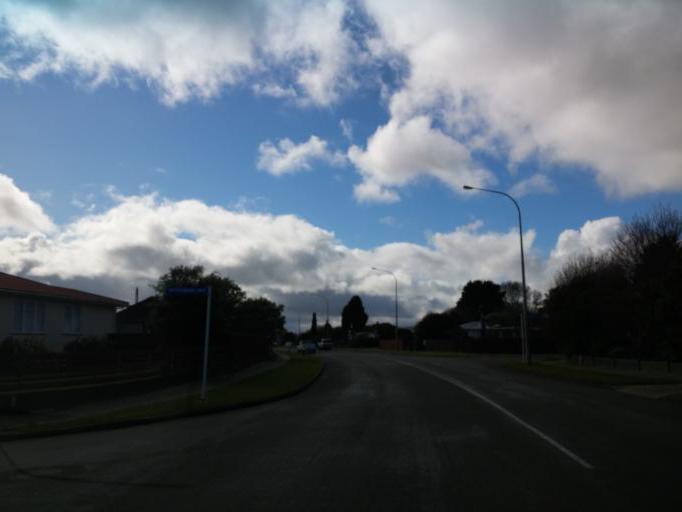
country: NZ
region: Manawatu-Wanganui
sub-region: Palmerston North City
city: Palmerston North
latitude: -40.3707
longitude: 175.5894
